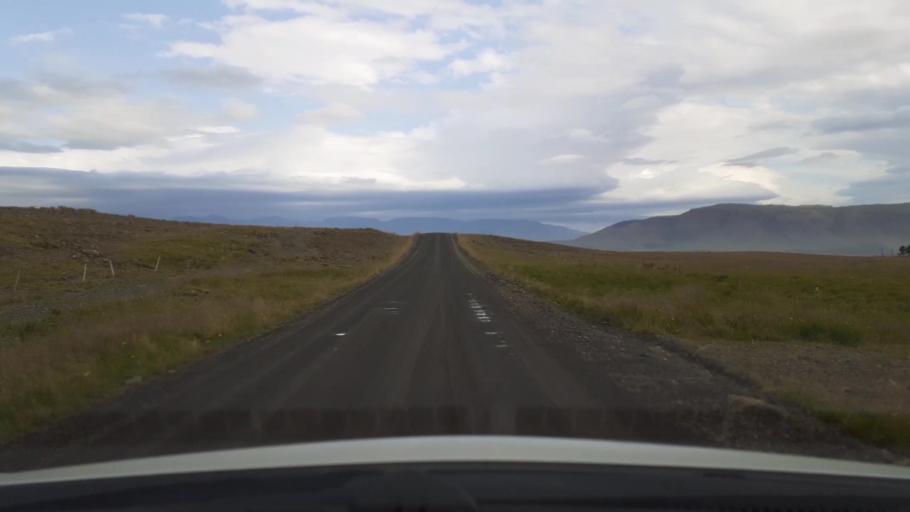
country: IS
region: Capital Region
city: Mosfellsbaer
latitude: 64.3127
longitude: -21.6520
